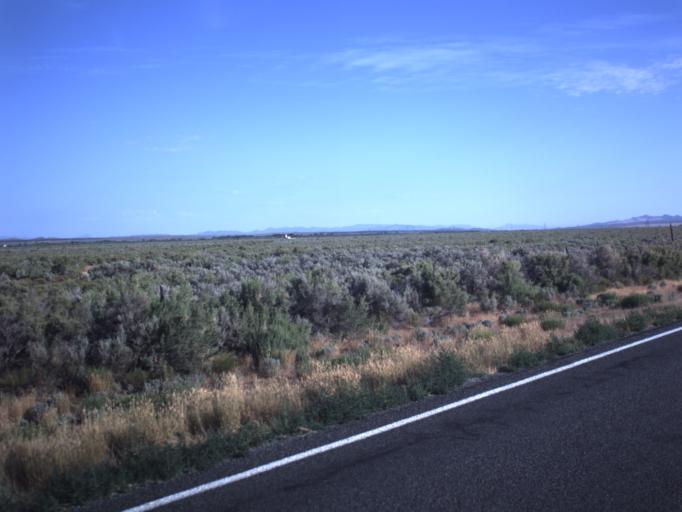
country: US
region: Utah
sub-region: Iron County
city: Enoch
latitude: 37.7752
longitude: -113.0552
